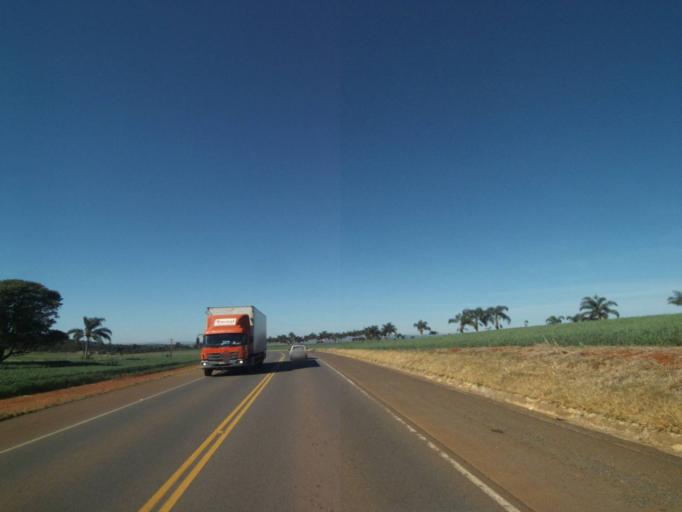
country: BR
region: Parana
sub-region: Tibagi
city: Tibagi
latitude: -24.4234
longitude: -50.3789
